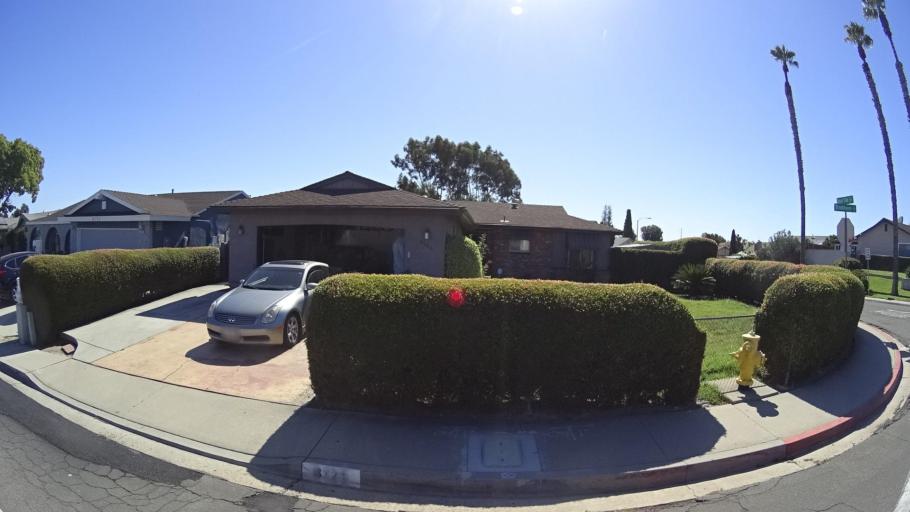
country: US
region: California
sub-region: San Diego County
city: La Presa
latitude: 32.7013
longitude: -117.0266
